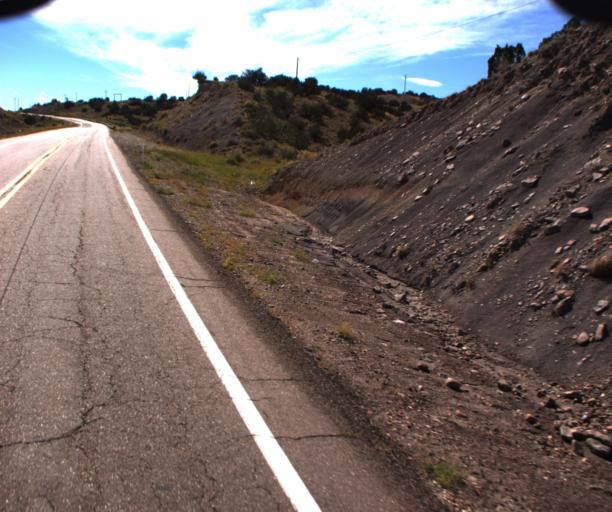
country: US
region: Arizona
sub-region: Apache County
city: Saint Johns
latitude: 34.4610
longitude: -109.6198
